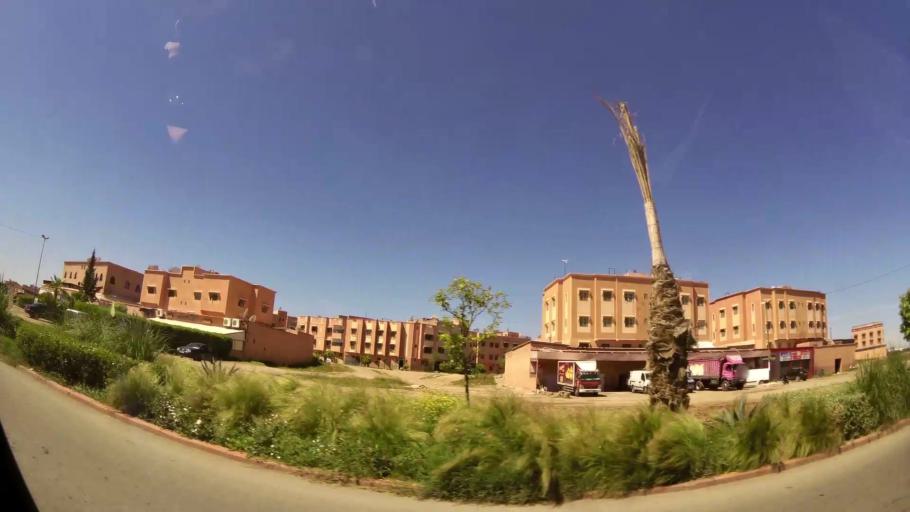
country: MA
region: Marrakech-Tensift-Al Haouz
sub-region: Marrakech
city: Marrakesh
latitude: 31.6600
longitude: -7.9846
